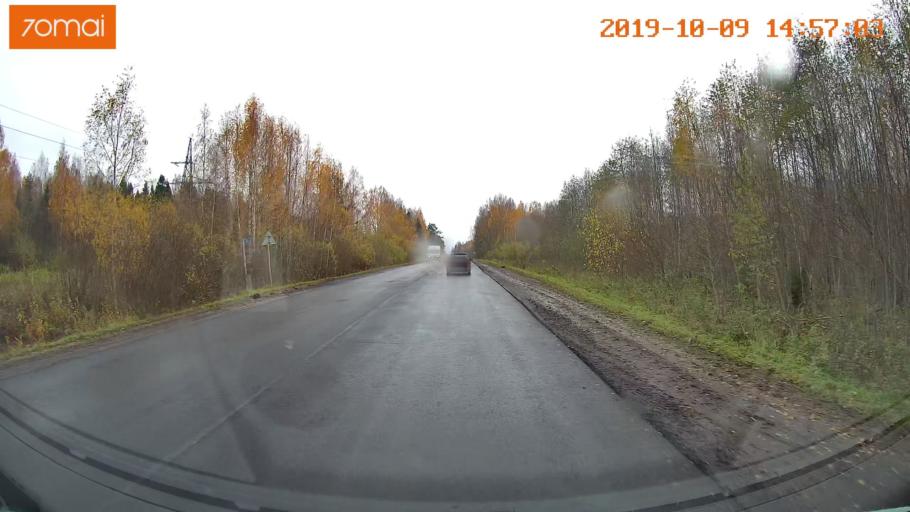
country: RU
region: Kostroma
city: Chistyye Bory
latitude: 58.3412
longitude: 41.6492
